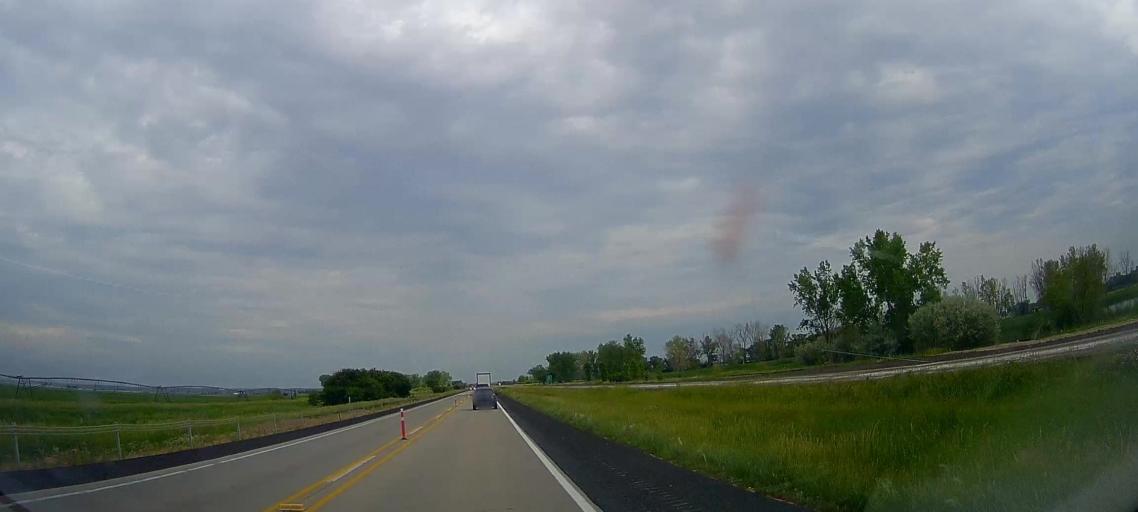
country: US
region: Iowa
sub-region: Harrison County
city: Missouri Valley
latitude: 41.6365
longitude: -96.0087
